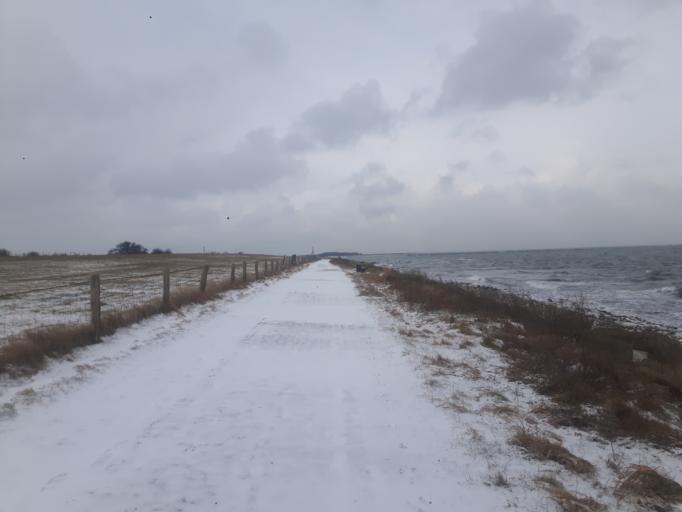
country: DE
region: Schleswig-Holstein
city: Fehmarn
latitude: 54.5050
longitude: 11.2140
